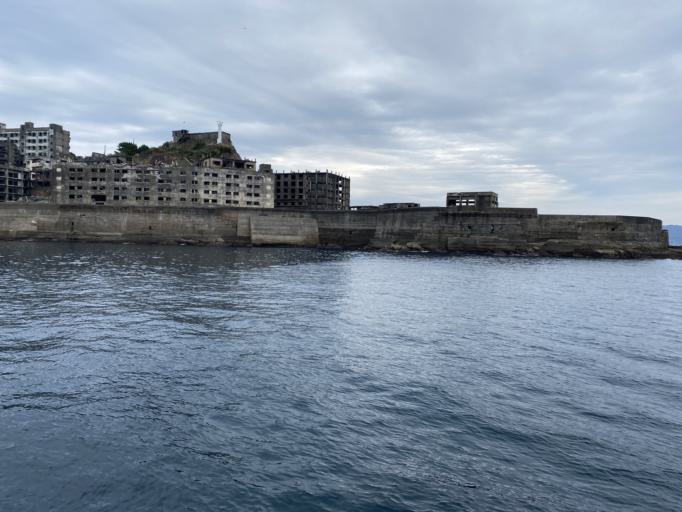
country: JP
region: Nagasaki
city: Nagasaki-shi
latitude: 32.6273
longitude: 129.7353
